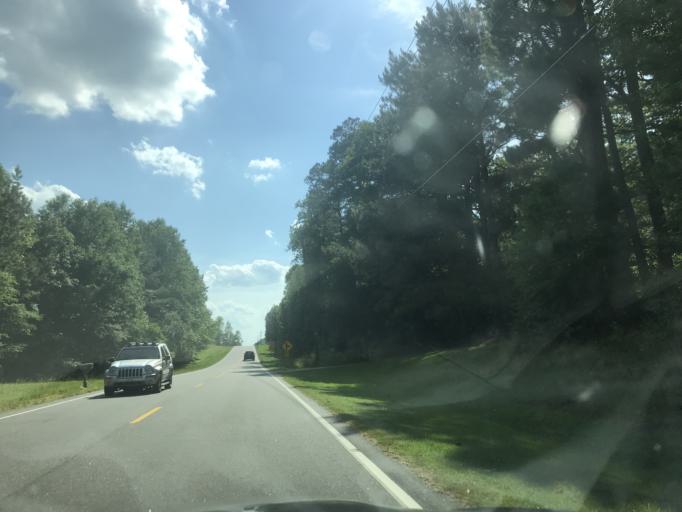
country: US
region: North Carolina
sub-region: Nash County
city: Spring Hope
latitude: 35.9566
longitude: -78.0786
